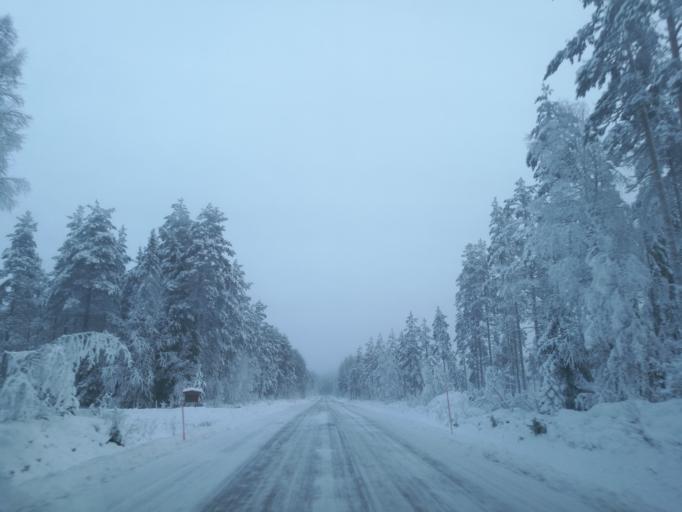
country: NO
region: Hedmark
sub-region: Grue
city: Kirkenaer
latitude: 60.4629
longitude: 12.5371
